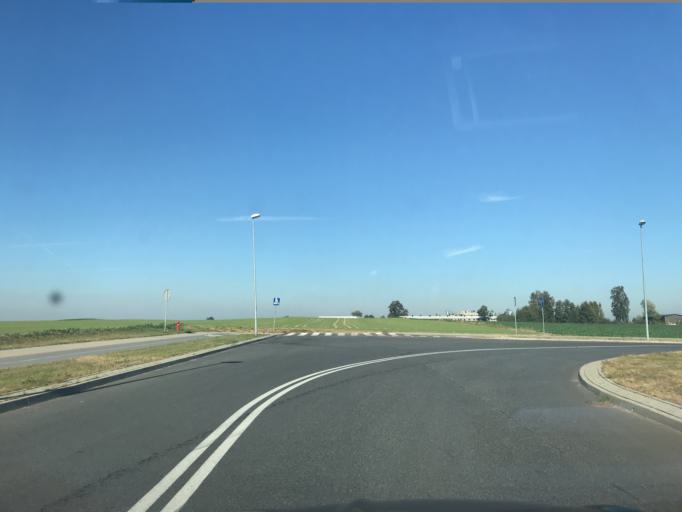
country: PL
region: Warmian-Masurian Voivodeship
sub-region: Powiat ilawski
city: Lubawa
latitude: 53.5153
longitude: 19.7249
